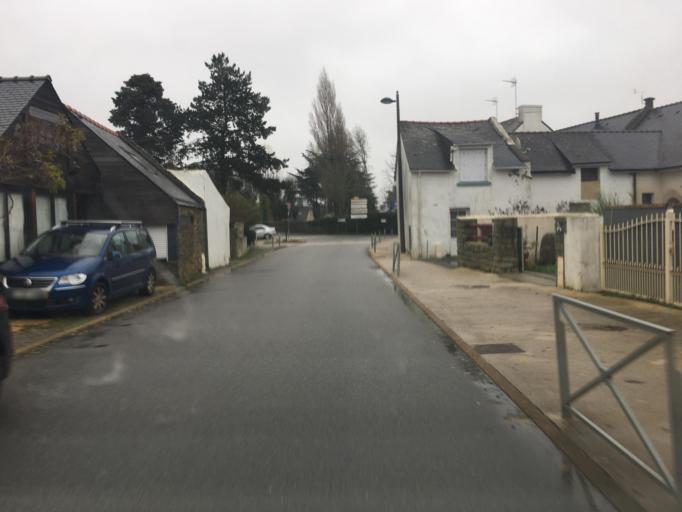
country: FR
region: Brittany
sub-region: Departement du Morbihan
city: Sarzeau
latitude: 47.5059
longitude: -2.6841
